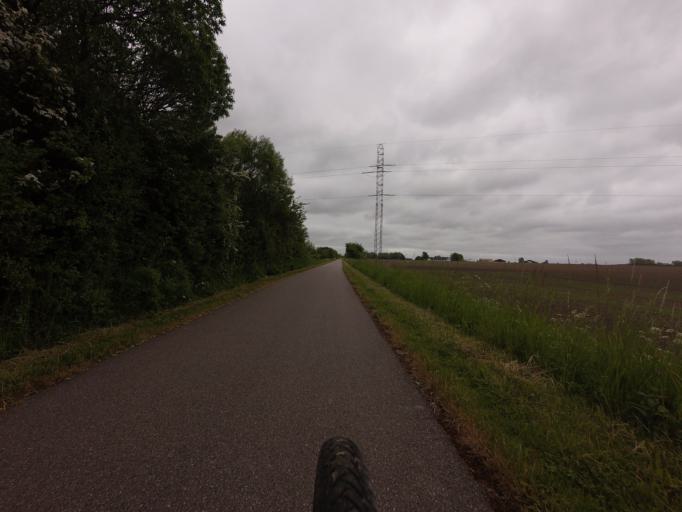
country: DK
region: Zealand
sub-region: Slagelse Kommune
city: Skaelskor
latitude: 55.2484
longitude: 11.3180
